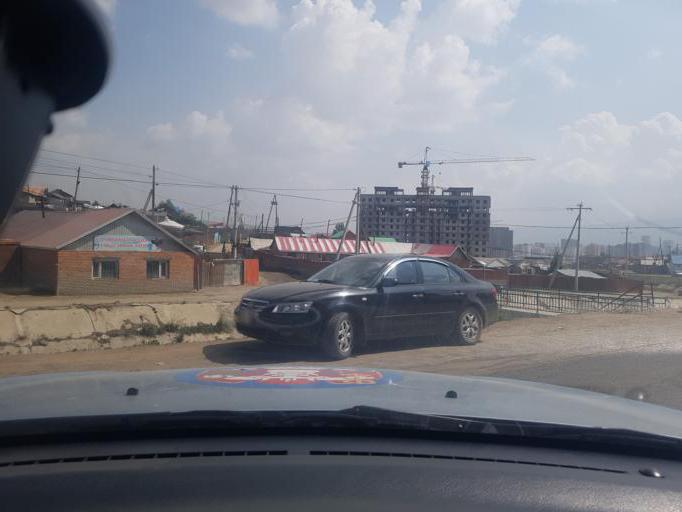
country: MN
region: Ulaanbaatar
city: Ulaanbaatar
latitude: 47.9390
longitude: 106.8979
